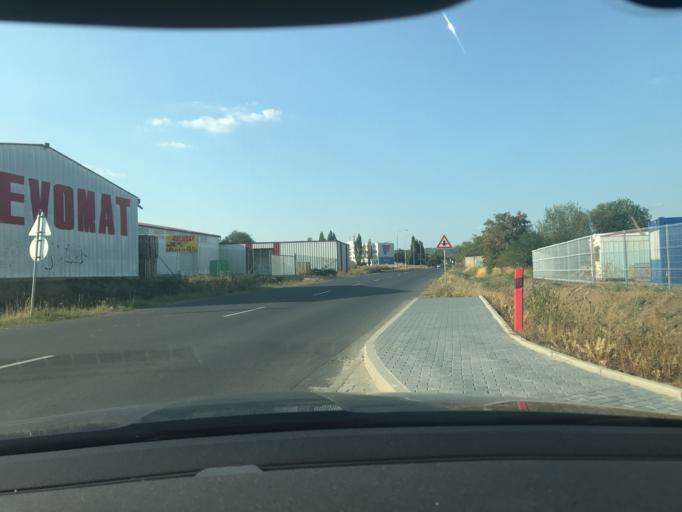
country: CZ
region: Ustecky
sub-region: Okres Chomutov
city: Chomutov
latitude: 50.4431
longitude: 13.3965
